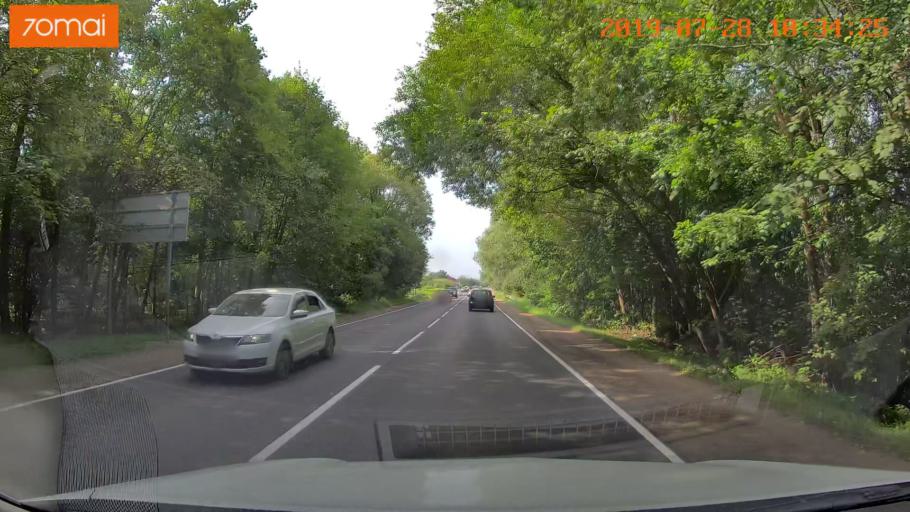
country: RU
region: Kaliningrad
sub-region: Gorod Kaliningrad
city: Kaliningrad
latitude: 54.7536
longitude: 20.4395
